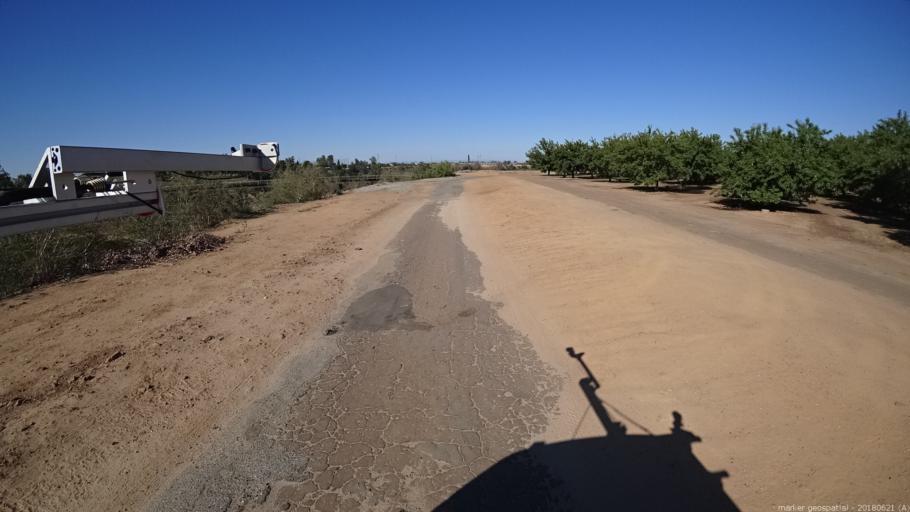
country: US
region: California
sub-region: Fresno County
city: Biola
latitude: 36.8512
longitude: -119.9057
